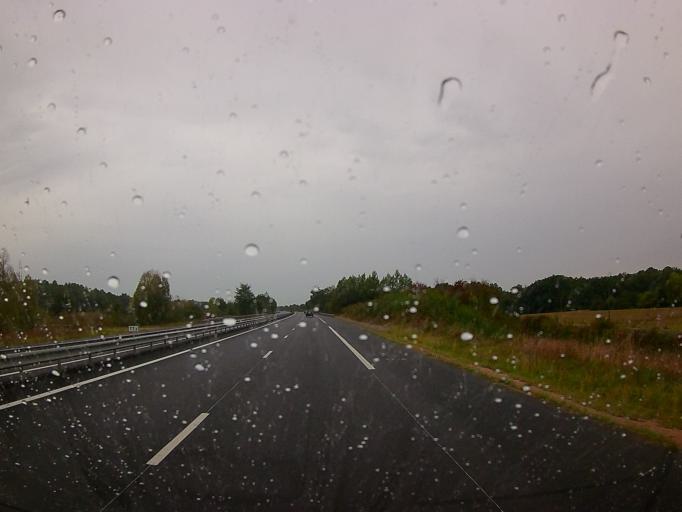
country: FR
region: Aquitaine
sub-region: Departement de la Dordogne
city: Saint-Medard-de-Mussidan
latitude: 45.0091
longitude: 0.3149
